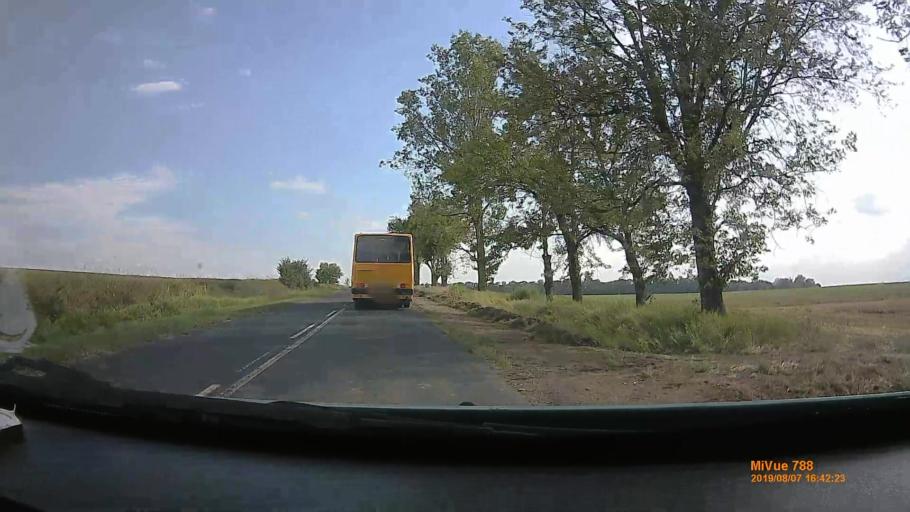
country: HU
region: Borsod-Abauj-Zemplen
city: Abaujszanto
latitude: 48.3698
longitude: 21.2157
